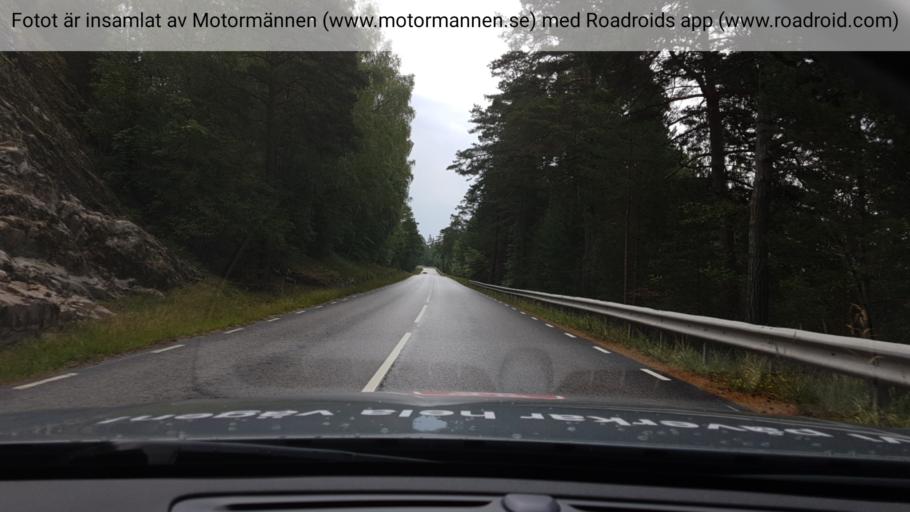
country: SE
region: Uppsala
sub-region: Habo Kommun
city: Balsta
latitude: 59.5471
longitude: 17.5584
